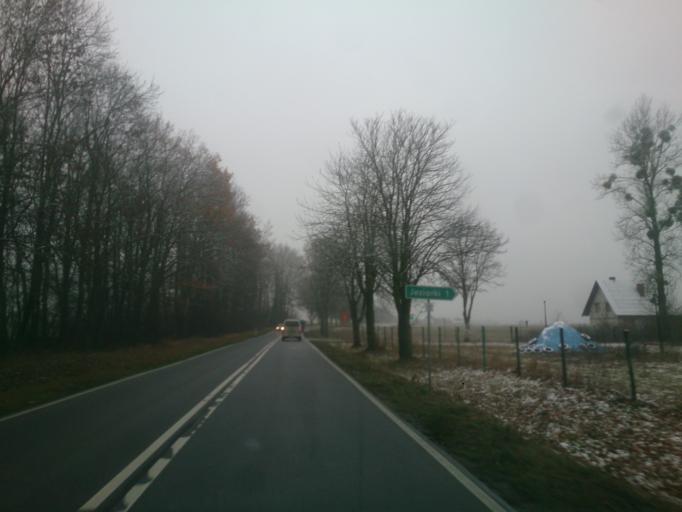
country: PL
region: Kujawsko-Pomorskie
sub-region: Powiat brodnicki
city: Brodnica
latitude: 53.1875
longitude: 19.3899
